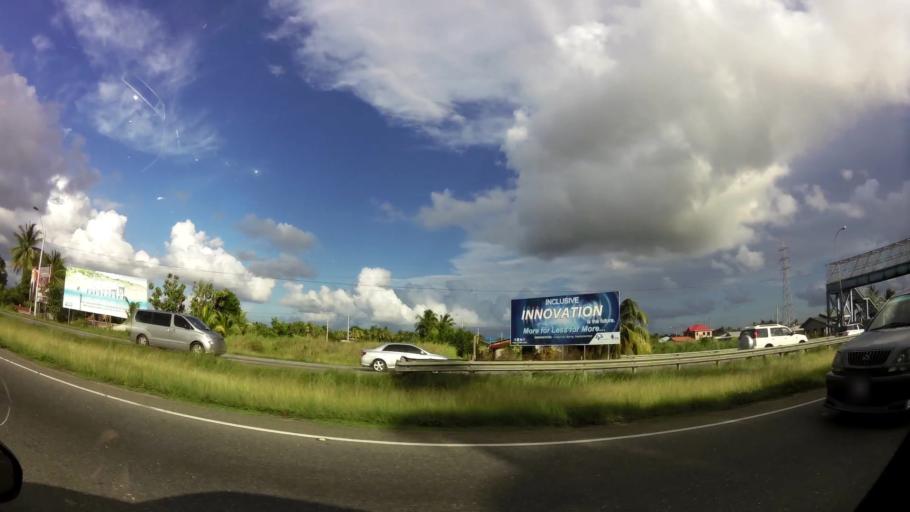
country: TT
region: Chaguanas
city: Chaguanas
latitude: 10.4966
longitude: -61.4065
